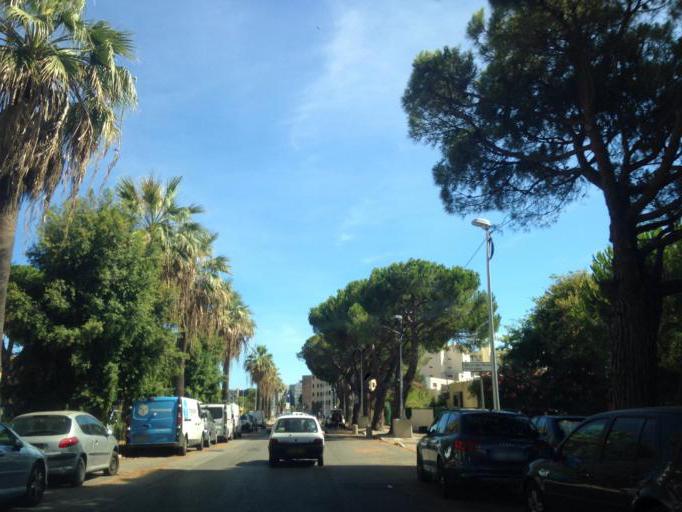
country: FR
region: Provence-Alpes-Cote d'Azur
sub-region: Departement des Alpes-Maritimes
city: Saint-Laurent-du-Var
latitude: 43.6730
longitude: 7.2089
